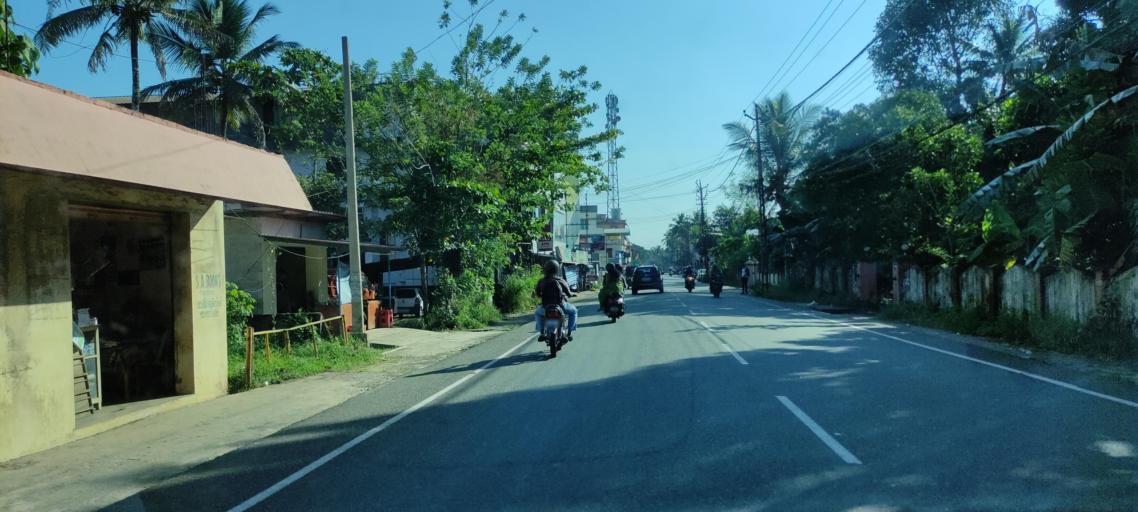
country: IN
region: Kerala
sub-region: Pattanamtitta
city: Pathanamthitta
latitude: 9.2477
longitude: 76.7574
